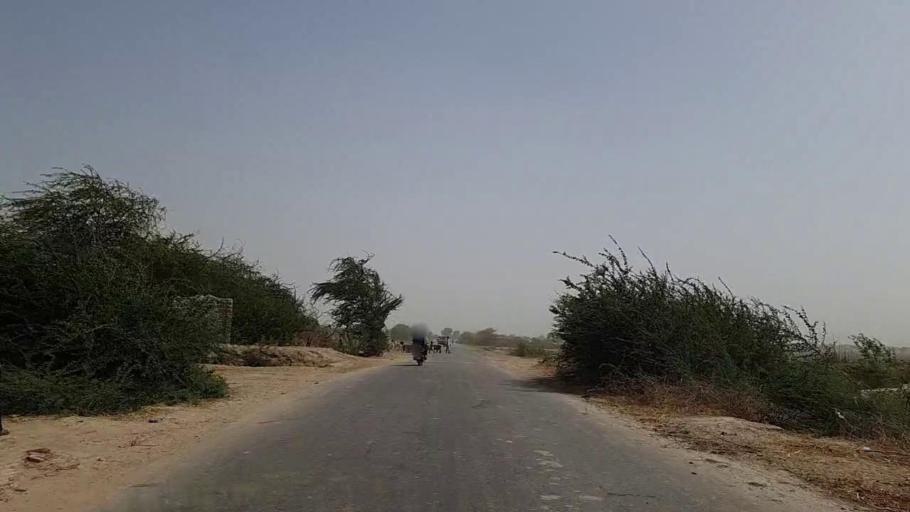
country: PK
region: Sindh
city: Talhar
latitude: 24.8759
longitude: 68.8358
